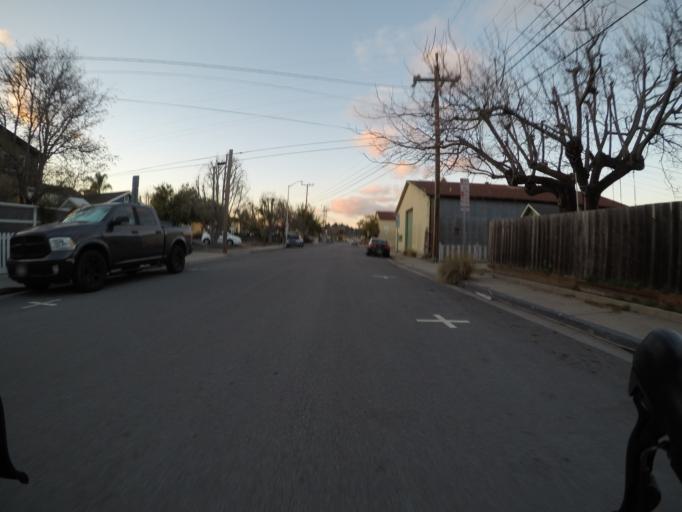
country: US
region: California
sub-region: Santa Cruz County
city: Santa Cruz
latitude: 36.9785
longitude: -122.0197
